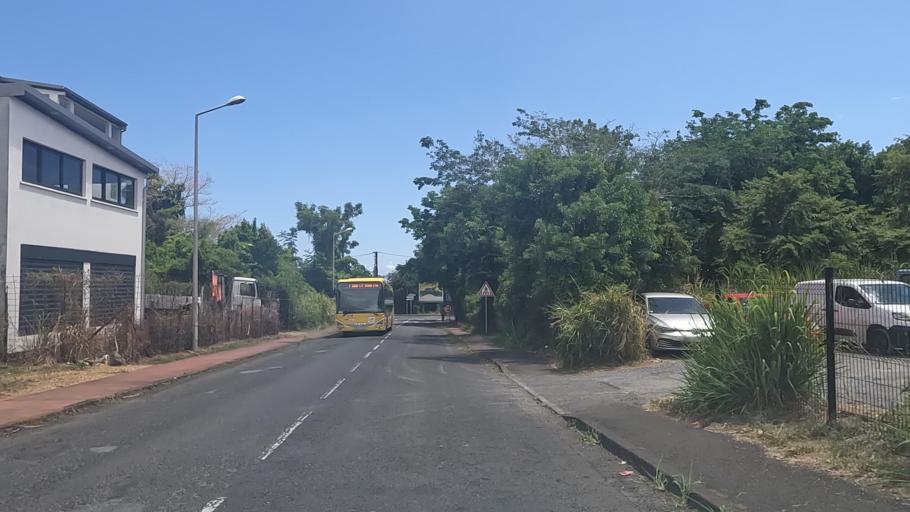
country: RE
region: Reunion
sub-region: Reunion
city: Saint-Benoit
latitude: -21.0312
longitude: 55.7091
